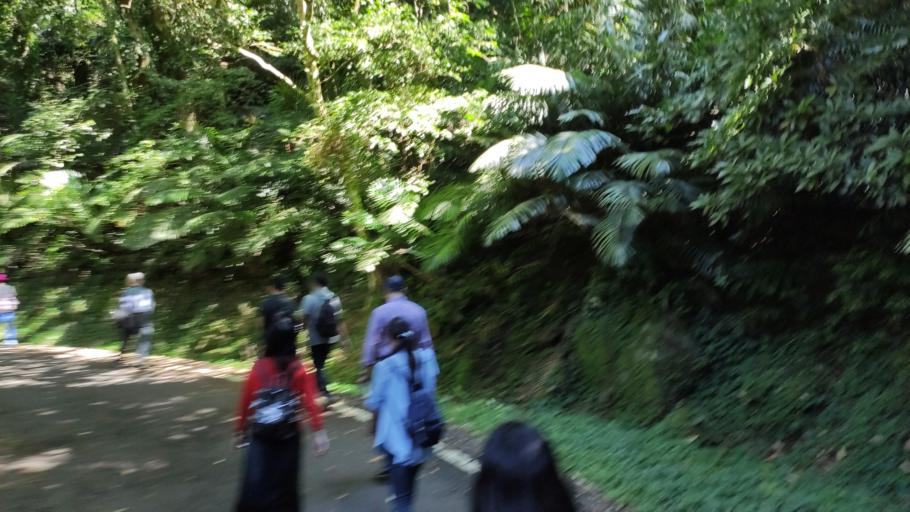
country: TW
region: Taiwan
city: Daxi
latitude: 24.8385
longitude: 121.3074
